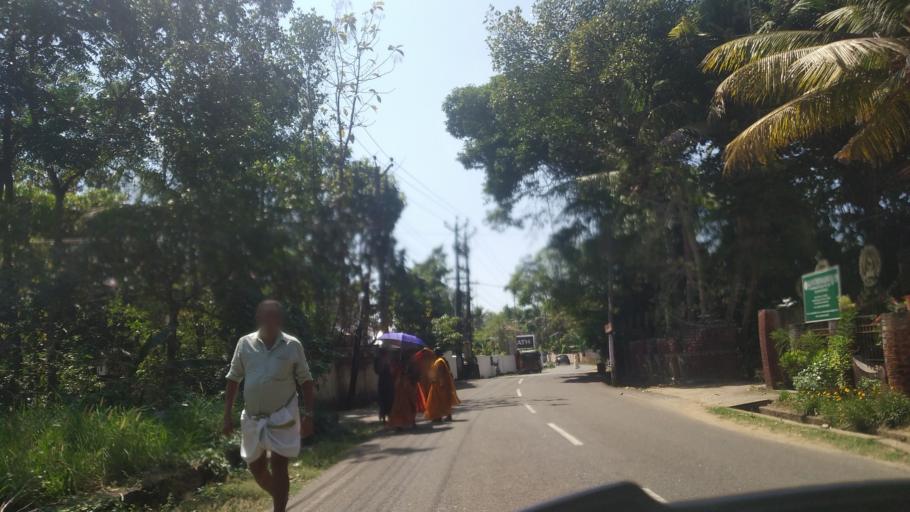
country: IN
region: Kerala
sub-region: Ernakulam
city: Elur
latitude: 10.1335
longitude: 76.2388
